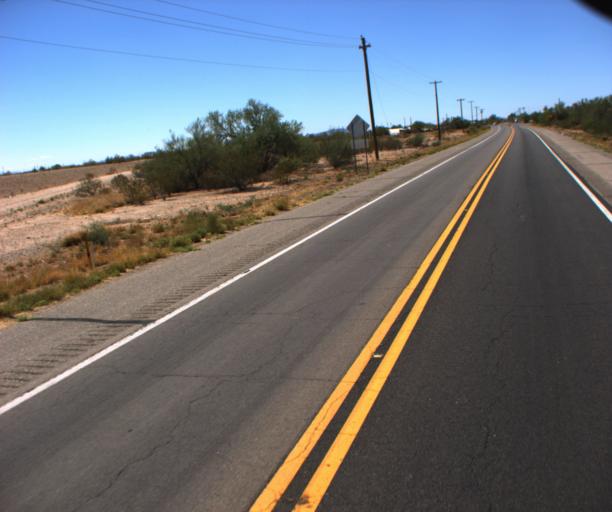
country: US
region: Arizona
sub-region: Pinal County
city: Maricopa
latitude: 32.8789
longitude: -112.0493
